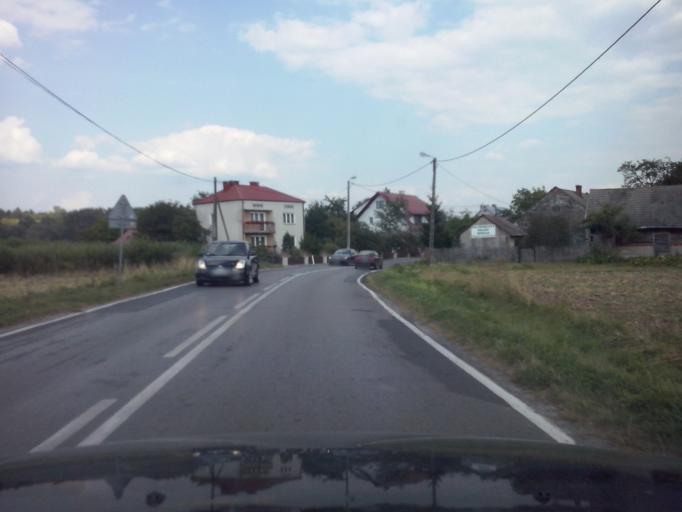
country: PL
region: Subcarpathian Voivodeship
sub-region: Powiat nizanski
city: Krzeszow
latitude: 50.4020
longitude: 22.3251
